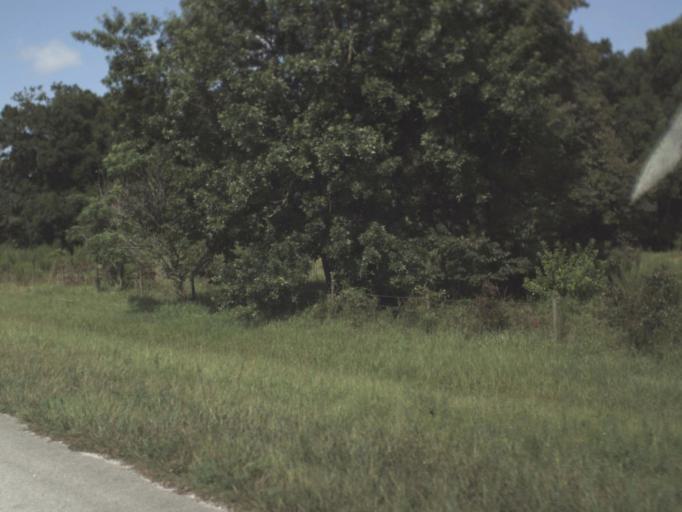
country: US
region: Florida
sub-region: Hernando County
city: North Brooksville
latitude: 28.6096
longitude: -82.4082
